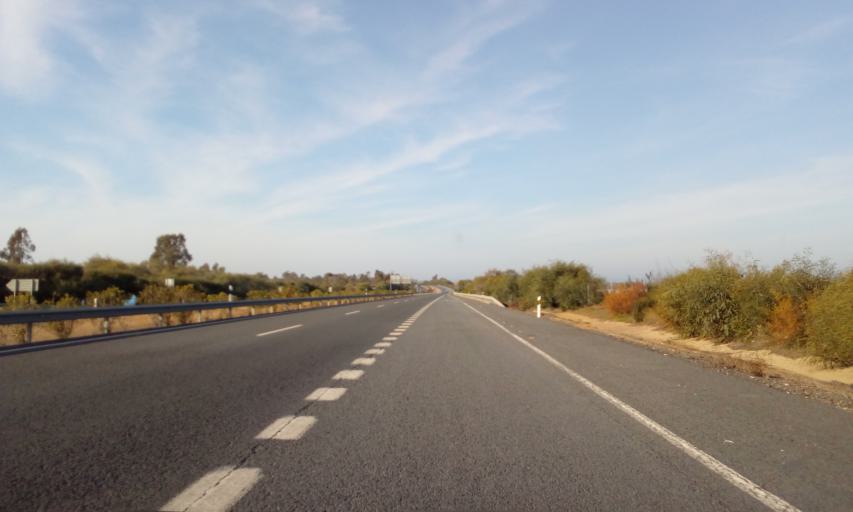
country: ES
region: Andalusia
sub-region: Provincia de Huelva
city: Villablanca
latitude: 37.2603
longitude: -7.3059
